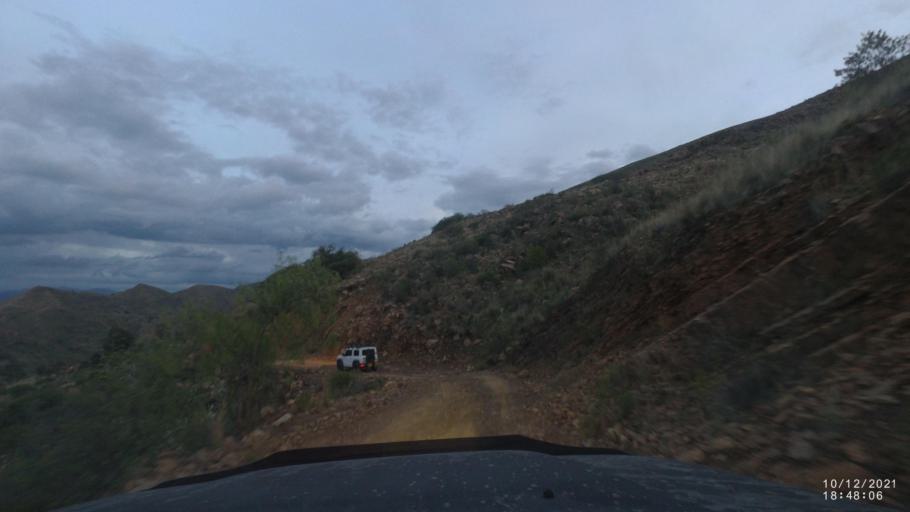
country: BO
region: Cochabamba
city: Tarata
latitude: -17.8812
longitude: -65.9744
